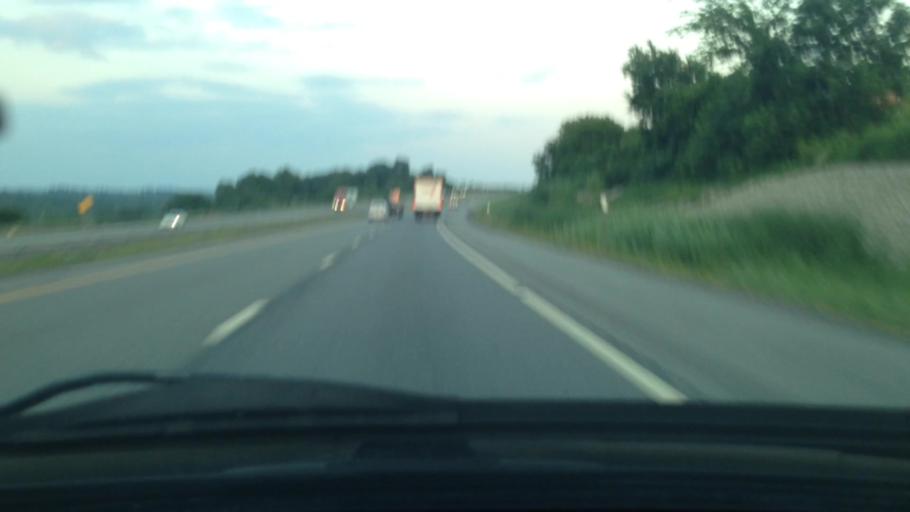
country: US
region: New York
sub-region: Montgomery County
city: Saint Johnsville
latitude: 42.9887
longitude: -74.6702
